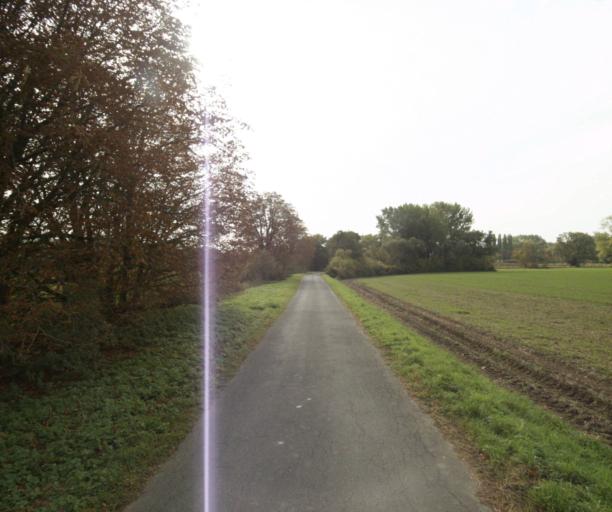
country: FR
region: Nord-Pas-de-Calais
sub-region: Departement du Nord
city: Don
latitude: 50.5451
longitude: 2.9025
